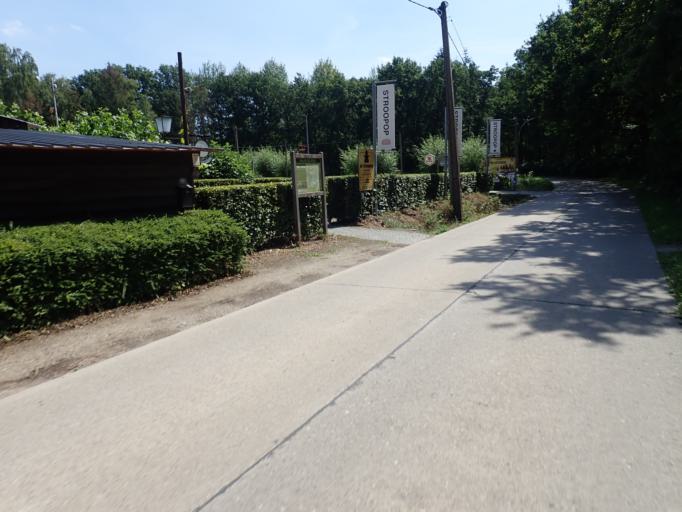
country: BE
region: Flanders
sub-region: Provincie Antwerpen
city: Zandhoven
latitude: 51.2268
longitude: 4.6395
